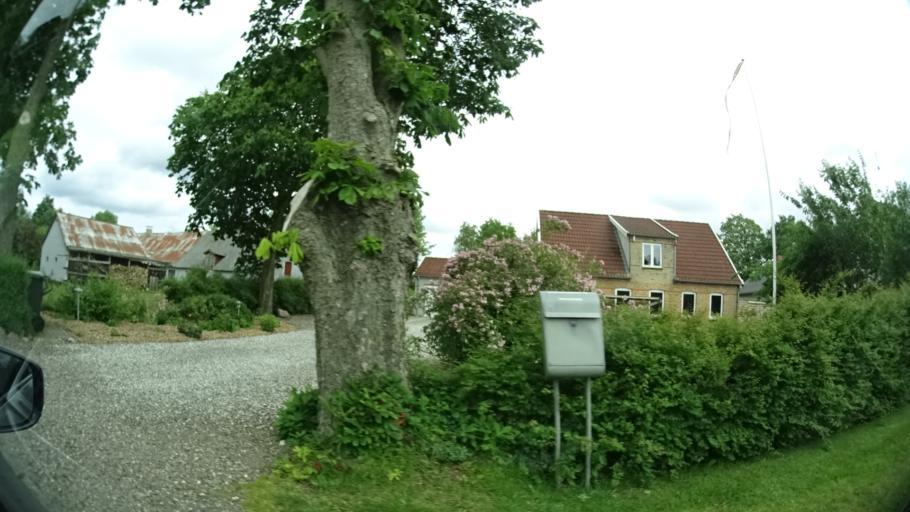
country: DK
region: Central Jutland
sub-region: Norddjurs Kommune
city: Grenaa
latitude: 56.4717
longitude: 10.7162
